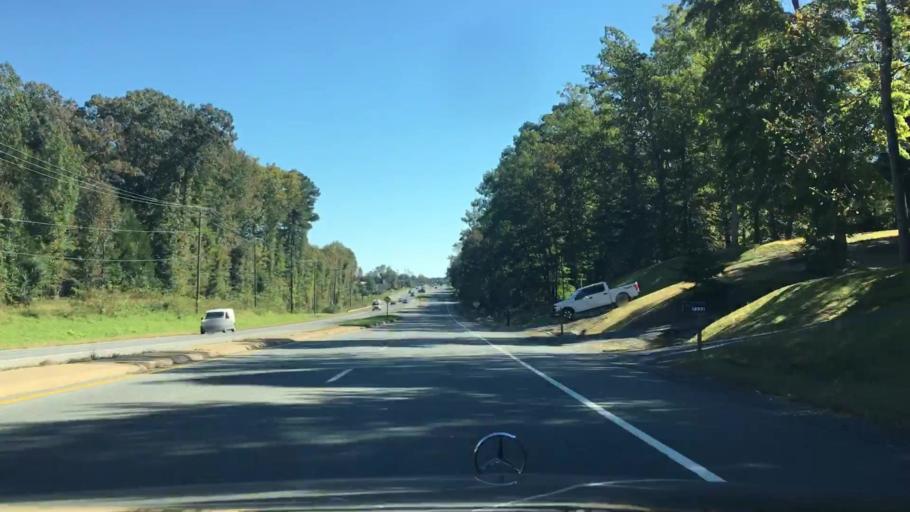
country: US
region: Virginia
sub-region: King George County
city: King George
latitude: 38.2793
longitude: -77.2169
